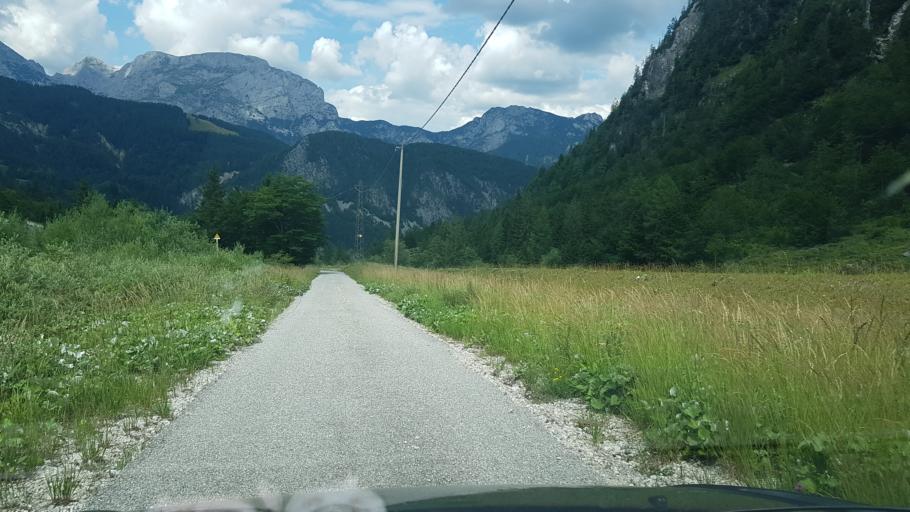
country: IT
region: Friuli Venezia Giulia
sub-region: Provincia di Udine
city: Pontebba
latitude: 46.4907
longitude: 13.2551
